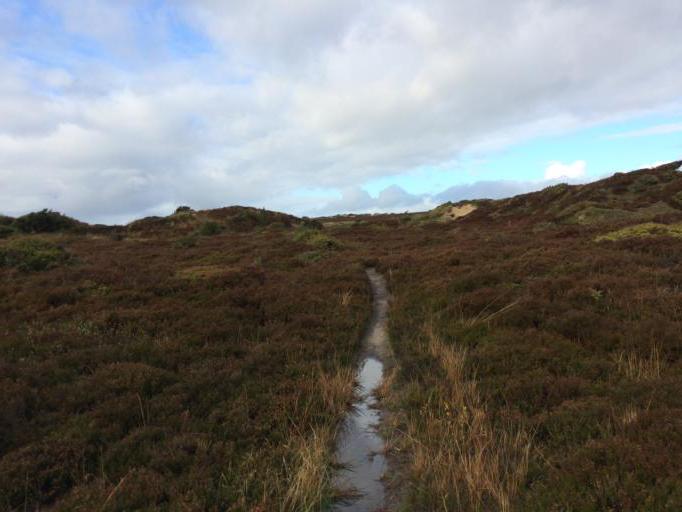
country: DK
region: Central Jutland
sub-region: Holstebro Kommune
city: Ulfborg
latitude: 56.2547
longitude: 8.4126
